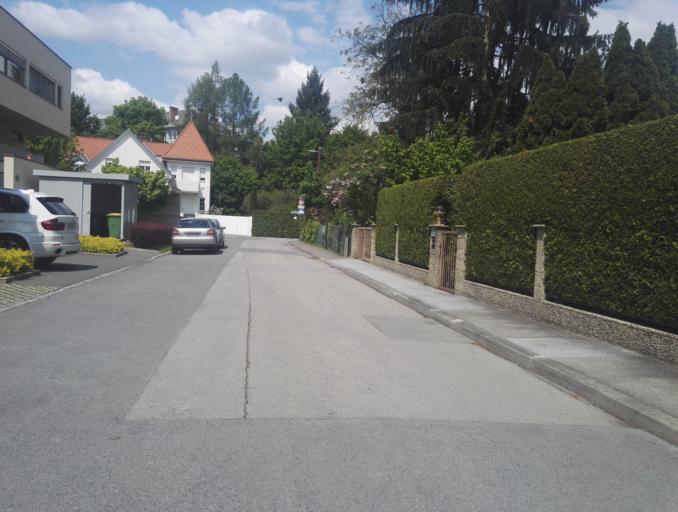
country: AT
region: Styria
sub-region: Graz Stadt
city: Graz
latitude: 47.0565
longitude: 15.4676
